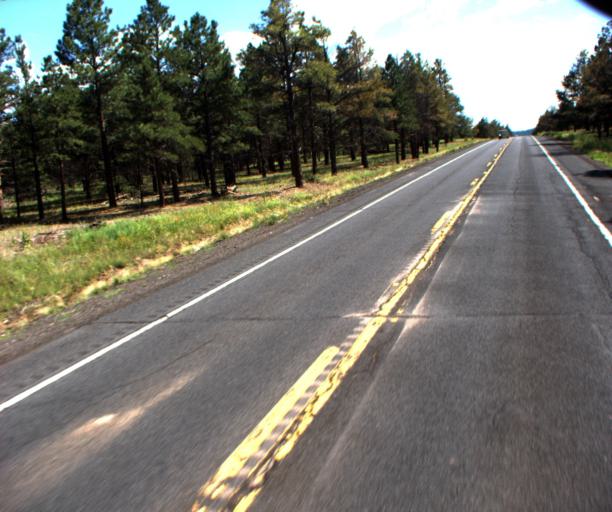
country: US
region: Arizona
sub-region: Coconino County
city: Williams
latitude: 35.2802
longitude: -112.1466
